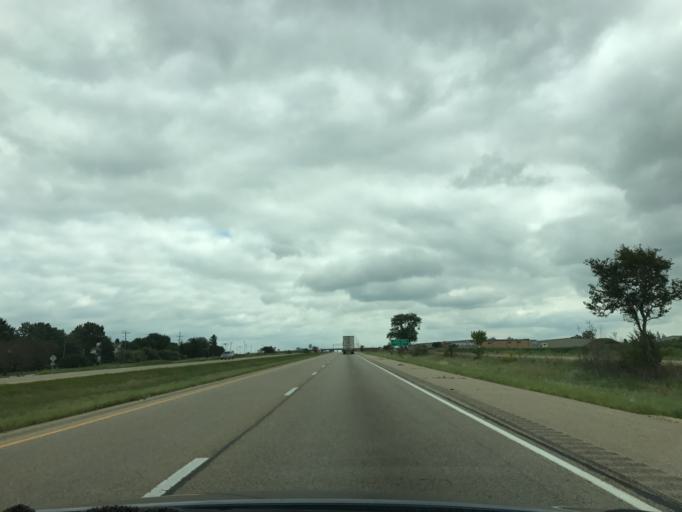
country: US
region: Illinois
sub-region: LaSalle County
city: Peru
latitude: 41.3646
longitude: -89.1636
